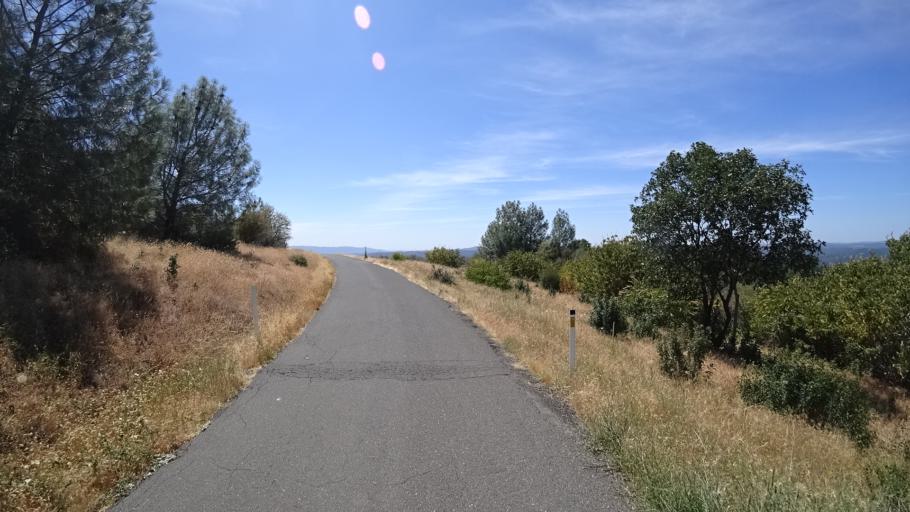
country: US
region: California
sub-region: Calaveras County
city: Forest Meadows
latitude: 38.1805
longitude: -120.4367
